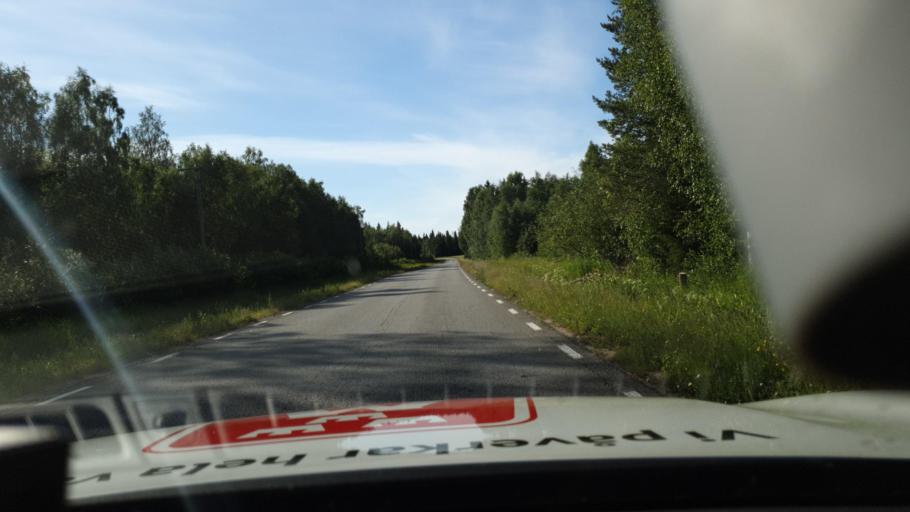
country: SE
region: Norrbotten
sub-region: Kalix Kommun
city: Toere
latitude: 65.8928
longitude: 22.6380
